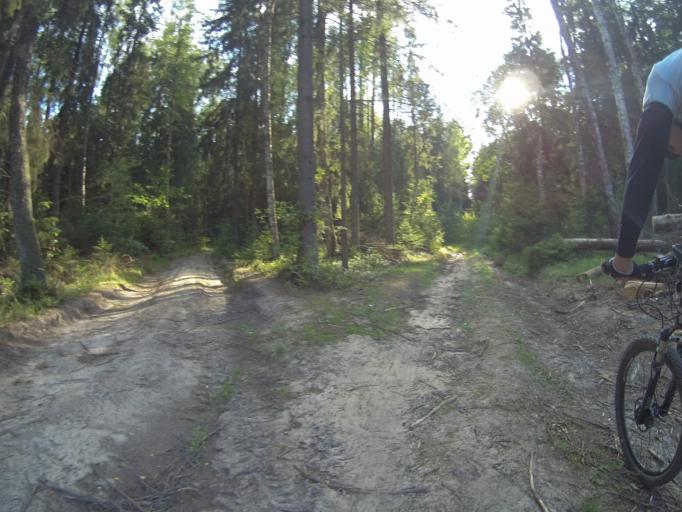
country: RU
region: Vladimir
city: Orgtrud
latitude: 56.1143
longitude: 40.5884
